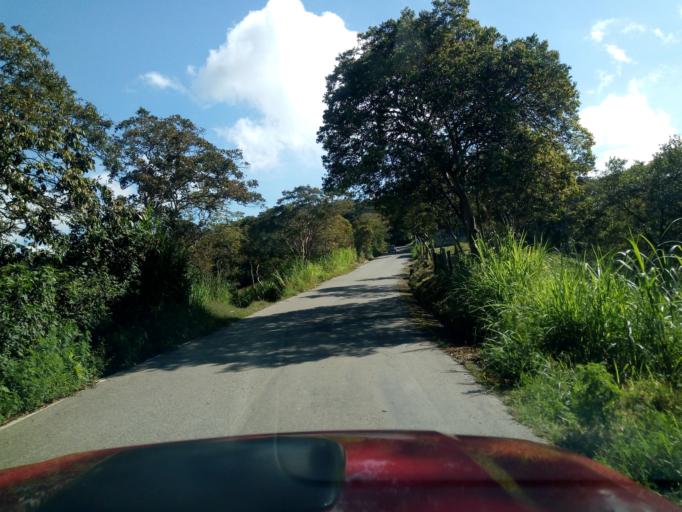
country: CO
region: Boyaca
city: Moniquira
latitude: 5.8738
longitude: -73.5522
